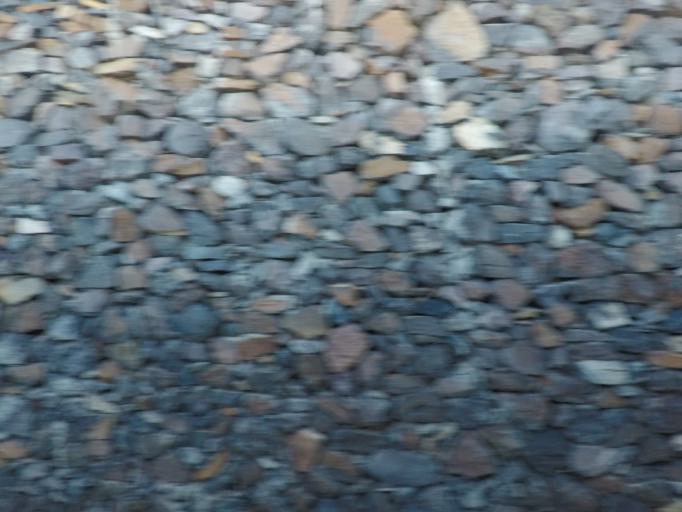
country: ES
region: Canary Islands
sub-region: Provincia de Santa Cruz de Tenerife
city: San Sebastian de la Gomera
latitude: 28.0835
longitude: -17.1329
